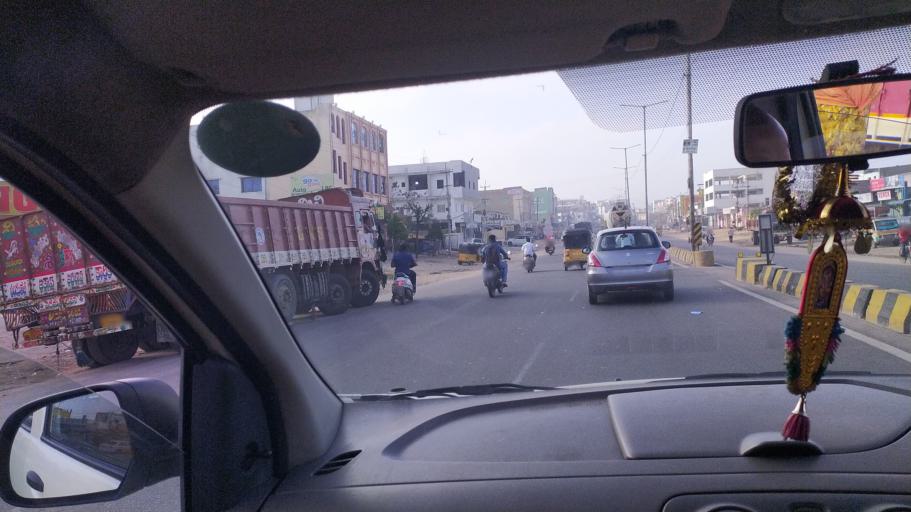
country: IN
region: Telangana
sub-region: Rangareddi
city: Balapur
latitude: 17.3199
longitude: 78.4672
